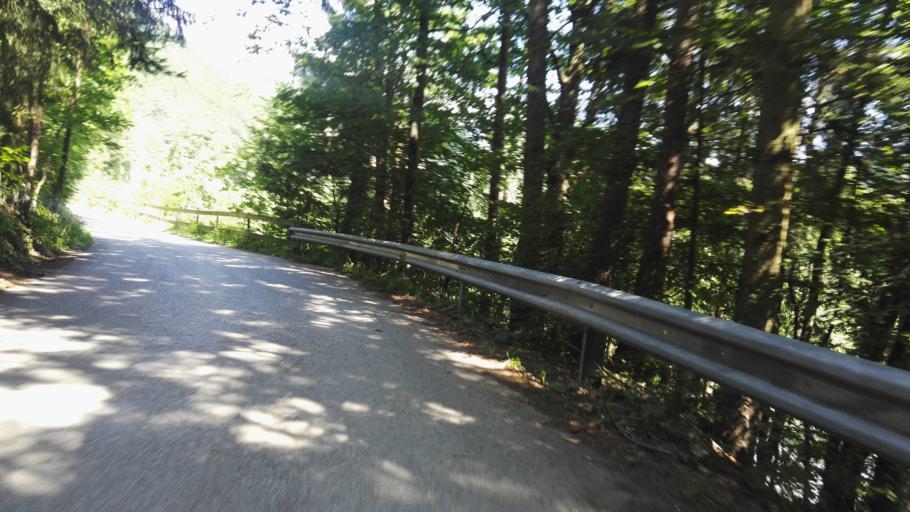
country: AT
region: Styria
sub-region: Politischer Bezirk Graz-Umgebung
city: Frohnleiten
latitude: 47.2373
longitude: 15.3121
